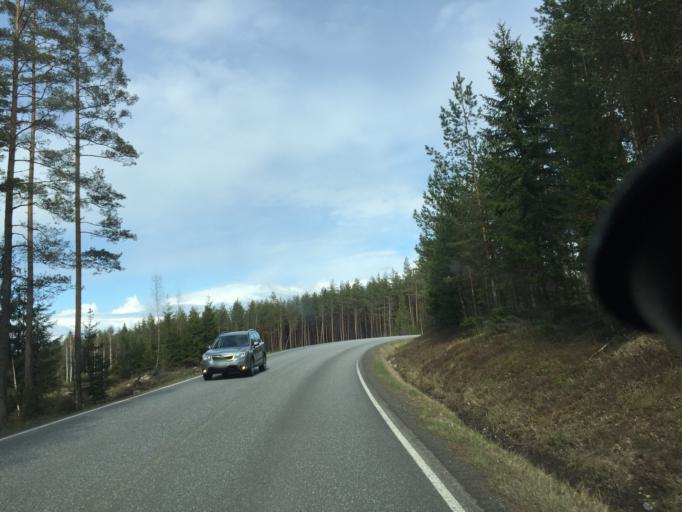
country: FI
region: Varsinais-Suomi
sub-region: Salo
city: Pernioe
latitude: 60.0194
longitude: 23.1693
